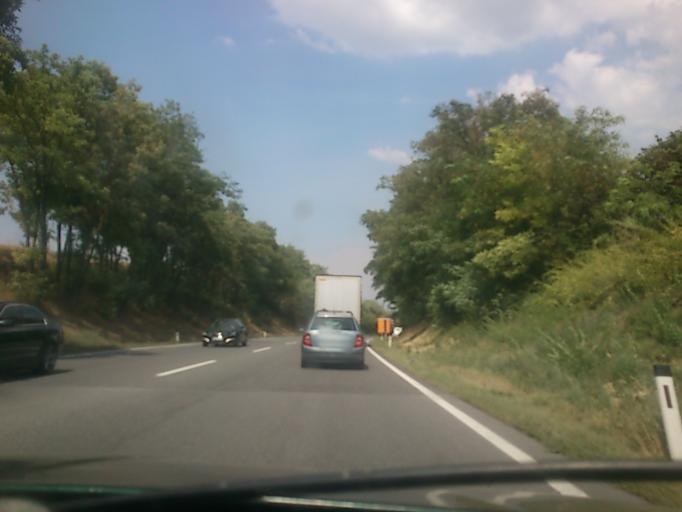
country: AT
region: Lower Austria
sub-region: Politischer Bezirk Mistelbach
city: Drasenhofen
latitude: 48.7340
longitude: 16.6562
